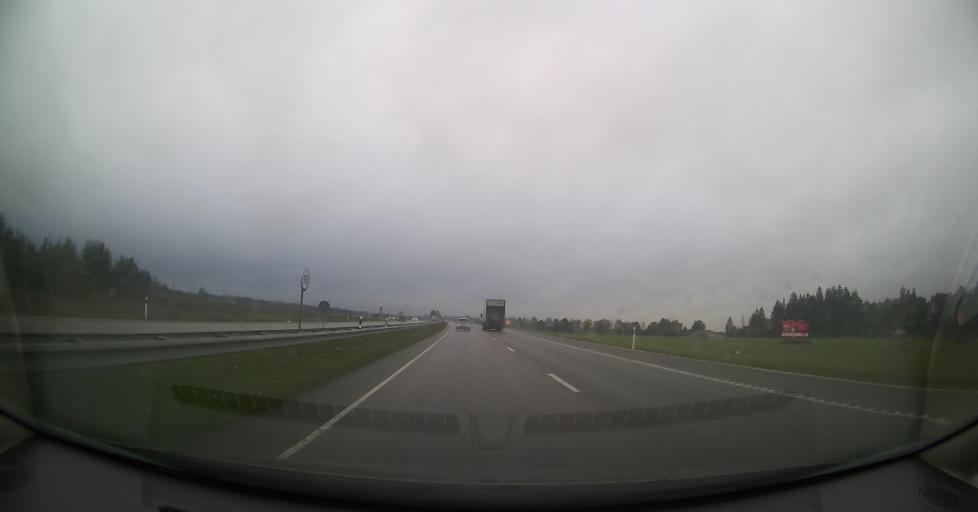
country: EE
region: Jaervamaa
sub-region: Paide linn
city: Paide
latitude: 58.9348
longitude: 25.6120
